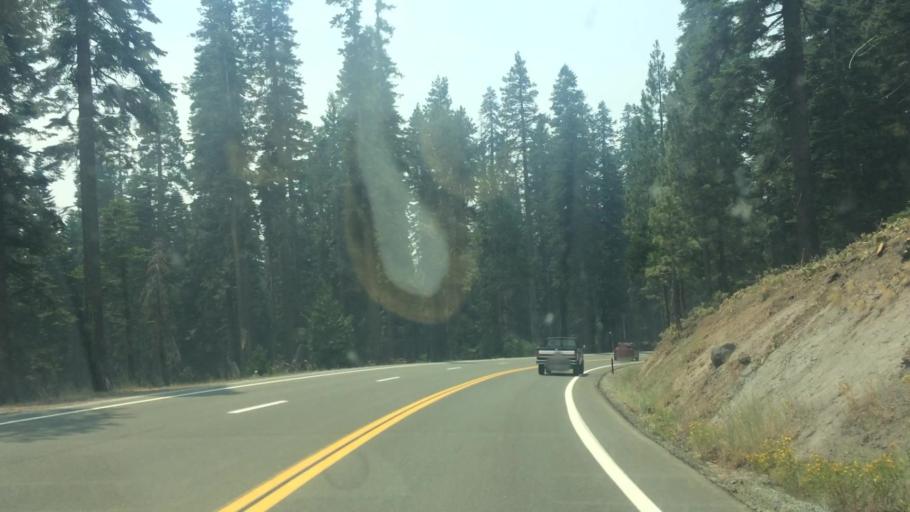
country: US
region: California
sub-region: Amador County
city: Pioneer
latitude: 38.5441
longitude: -120.3159
